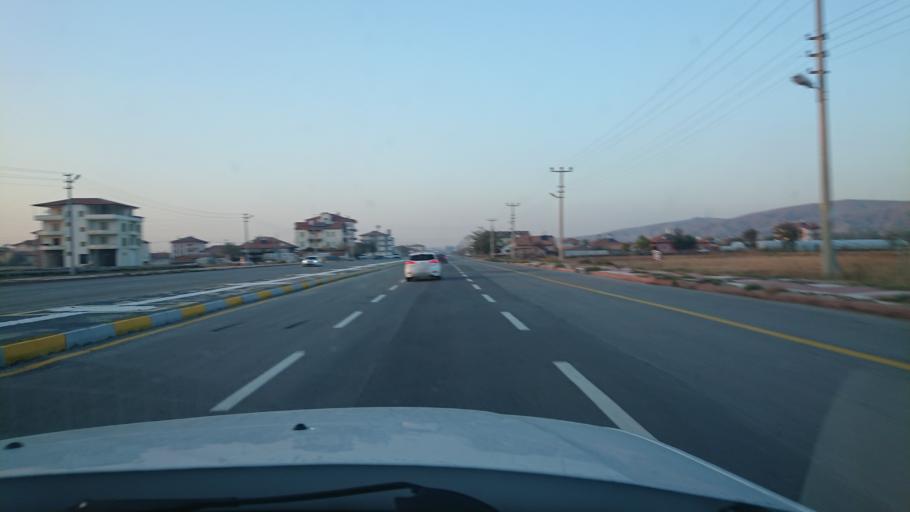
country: TR
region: Aksaray
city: Aksaray
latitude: 38.3359
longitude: 34.0484
